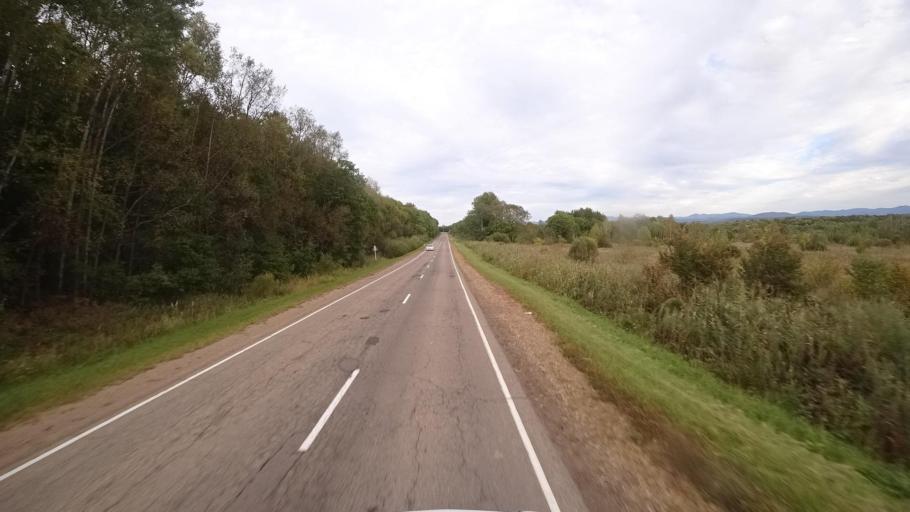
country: RU
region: Primorskiy
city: Yakovlevka
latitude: 44.3784
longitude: 133.4475
